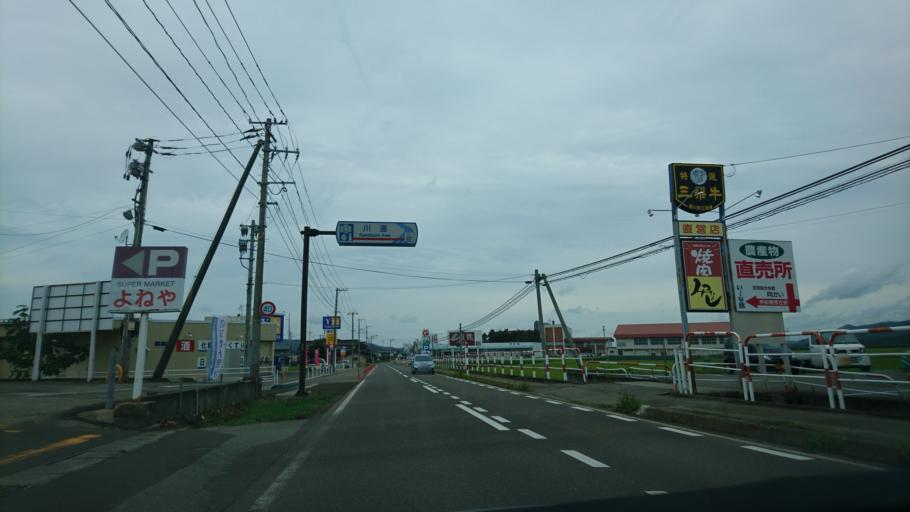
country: JP
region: Akita
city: Yuzawa
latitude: 39.1471
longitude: 140.5736
